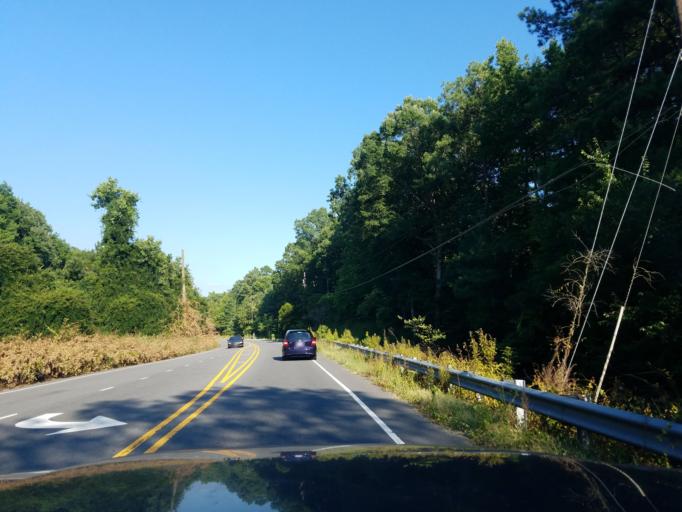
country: US
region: North Carolina
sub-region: Orange County
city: Chapel Hill
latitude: 35.8872
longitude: -78.9881
